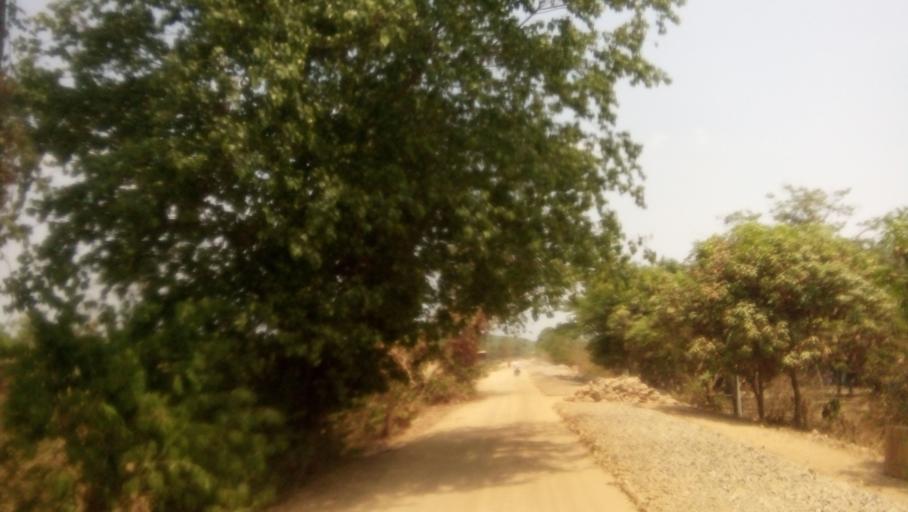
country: MM
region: Kayin
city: Hpa-an
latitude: 17.1570
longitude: 97.8024
